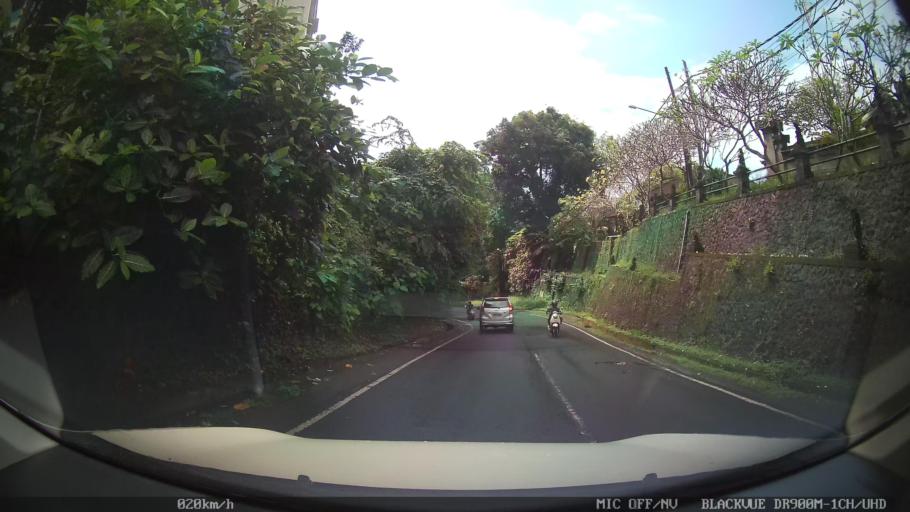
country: ID
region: Bali
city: Banjar Tebongkang
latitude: -8.5475
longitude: 115.2522
